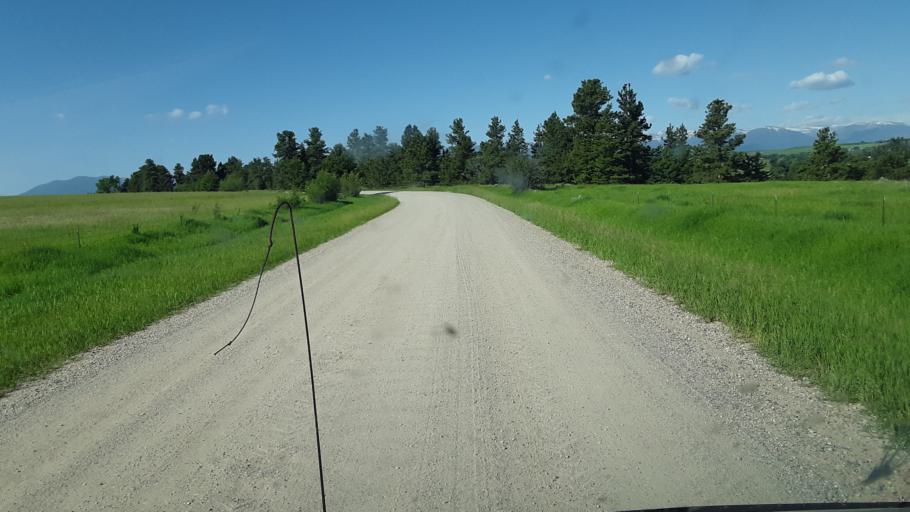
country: US
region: Montana
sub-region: Carbon County
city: Red Lodge
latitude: 45.3585
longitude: -109.1578
